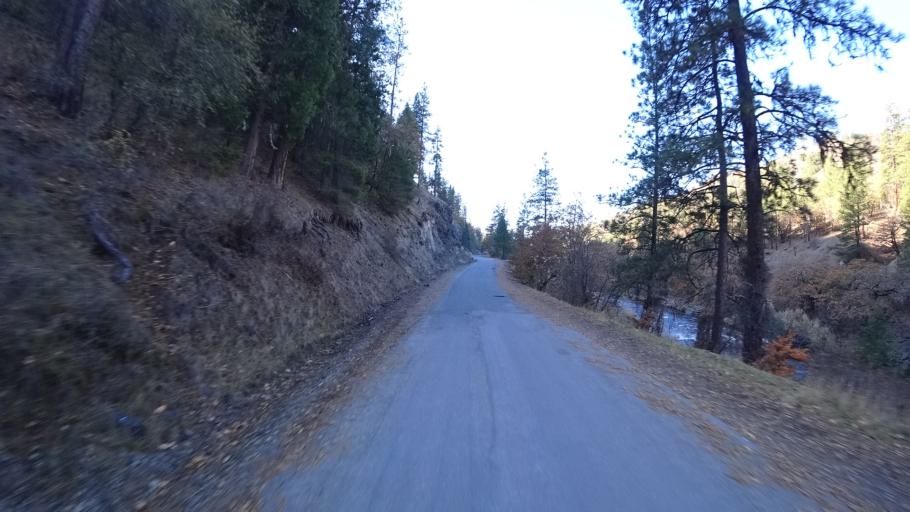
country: US
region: California
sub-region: Siskiyou County
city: Yreka
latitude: 41.8346
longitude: -122.9437
